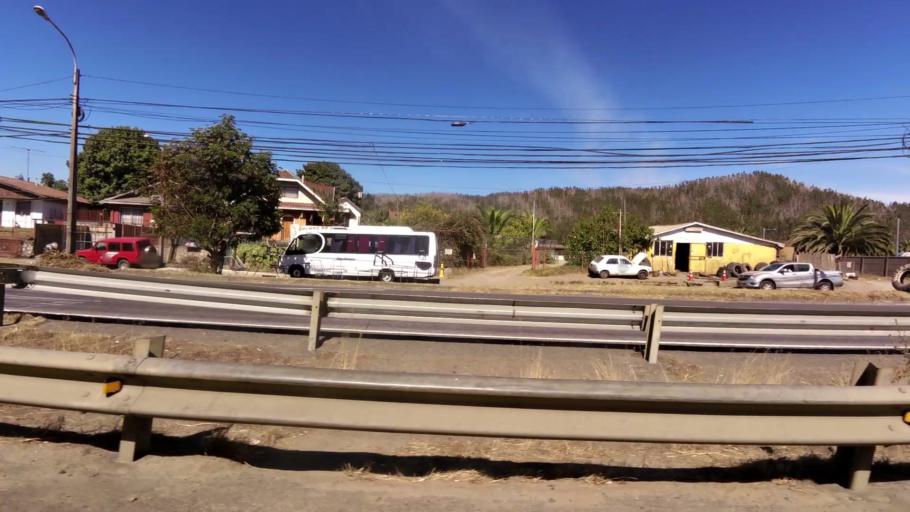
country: CL
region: Biobio
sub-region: Provincia de Concepcion
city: Concepcion
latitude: -36.7888
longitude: -73.0239
